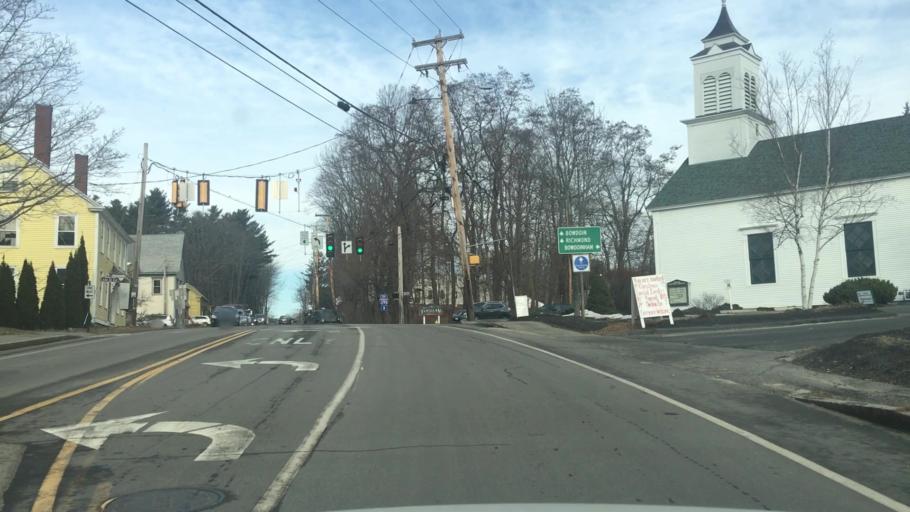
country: US
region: Maine
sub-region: Cumberland County
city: Brunswick
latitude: 43.9254
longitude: -69.9635
